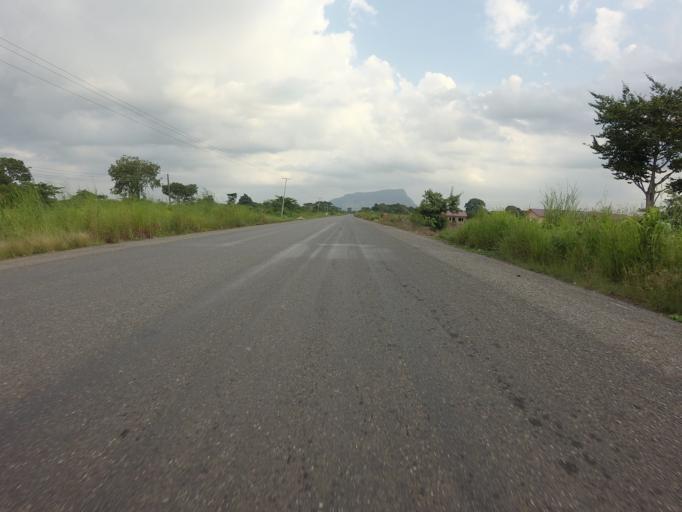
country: GH
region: Volta
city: Ho
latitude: 6.5691
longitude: 0.4858
